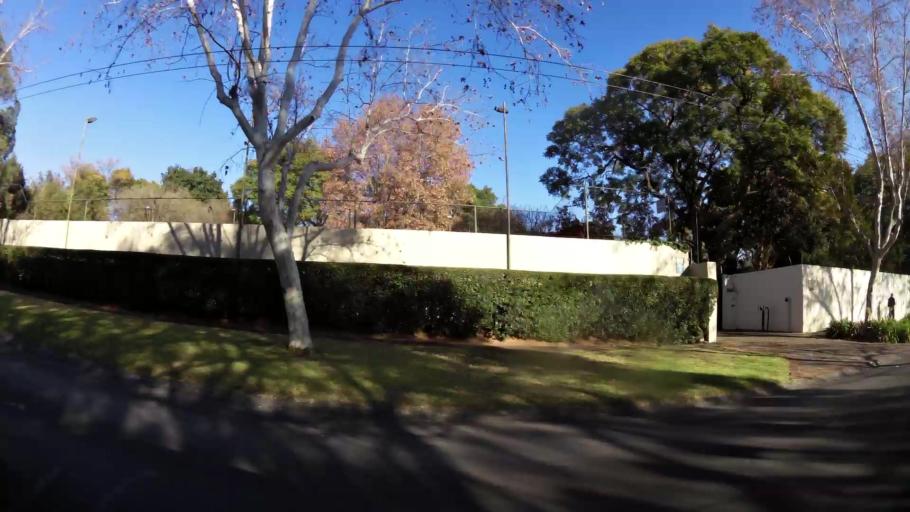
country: ZA
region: Gauteng
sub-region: City of Johannesburg Metropolitan Municipality
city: Johannesburg
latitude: -26.1507
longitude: 28.0652
